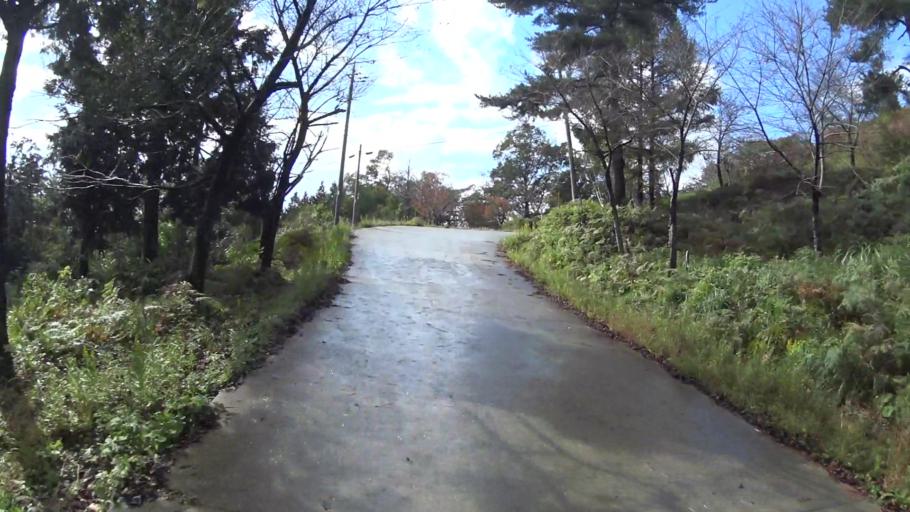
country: JP
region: Kyoto
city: Miyazu
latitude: 35.5998
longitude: 135.1872
